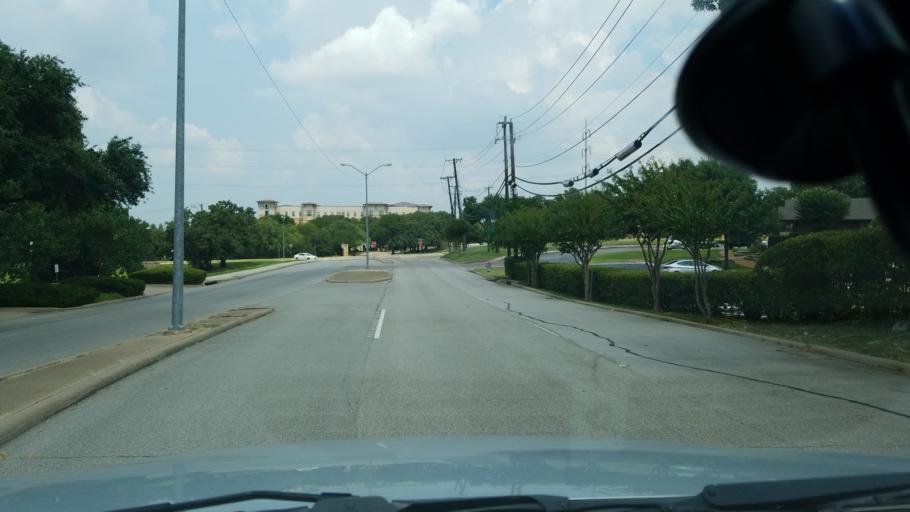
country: US
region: Texas
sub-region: Dallas County
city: Irving
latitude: 32.8429
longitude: -96.9223
